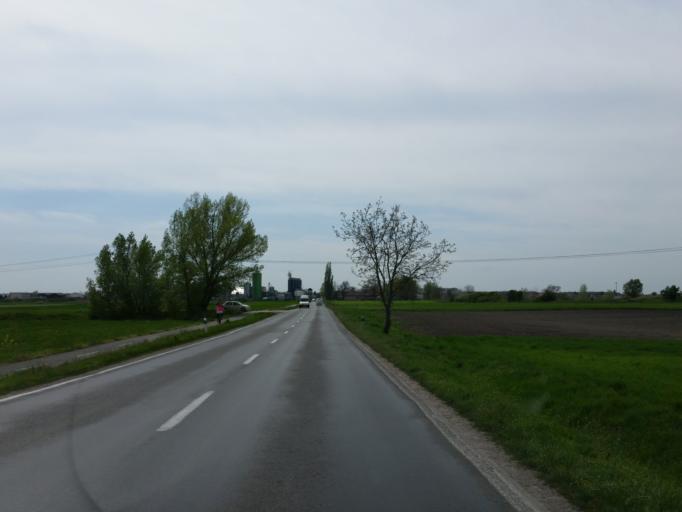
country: SK
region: Trnavsky
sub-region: Okres Dunajska Streda
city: Velky Meder
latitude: 47.8699
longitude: 17.7895
